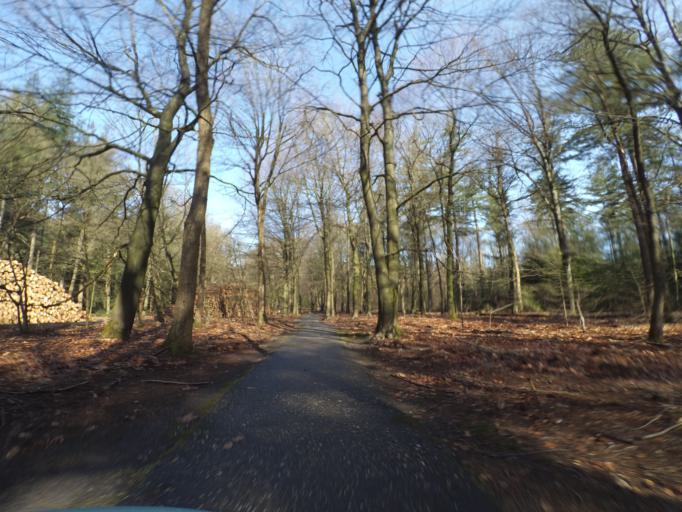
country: NL
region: Gelderland
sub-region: Gemeente Apeldoorn
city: Uddel
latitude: 52.2099
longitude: 5.8082
